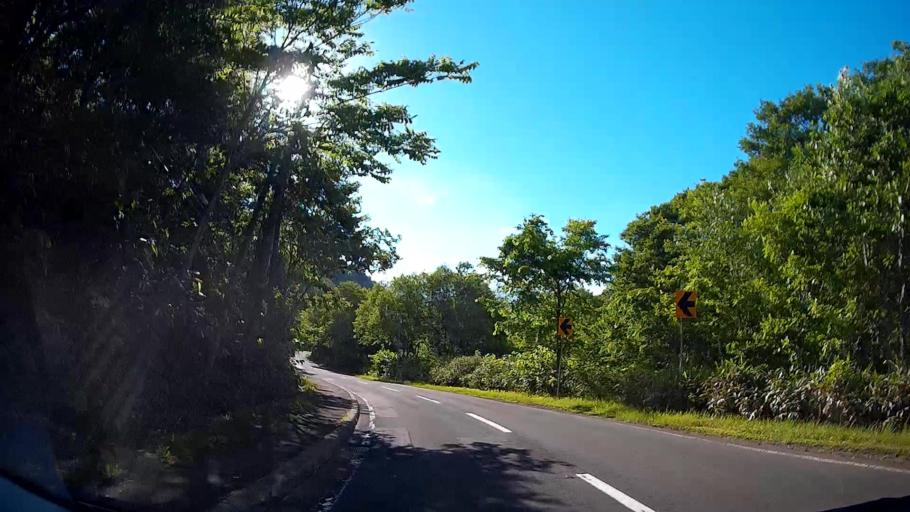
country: JP
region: Hokkaido
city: Sapporo
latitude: 42.9750
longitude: 141.1425
